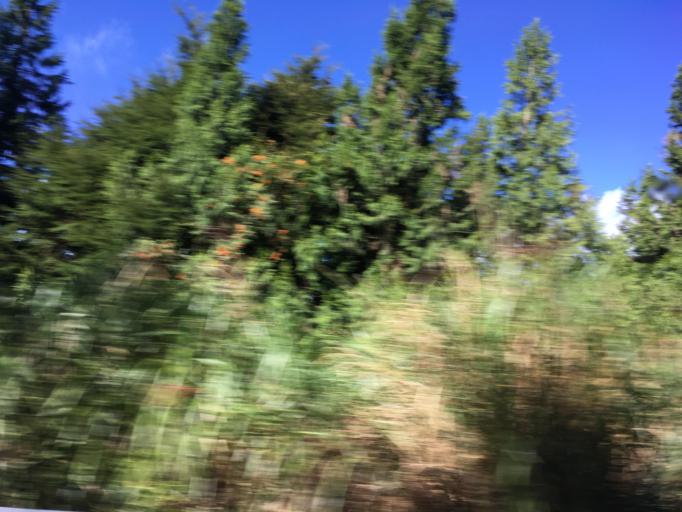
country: TW
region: Taiwan
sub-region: Yilan
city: Yilan
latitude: 24.5121
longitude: 121.5847
